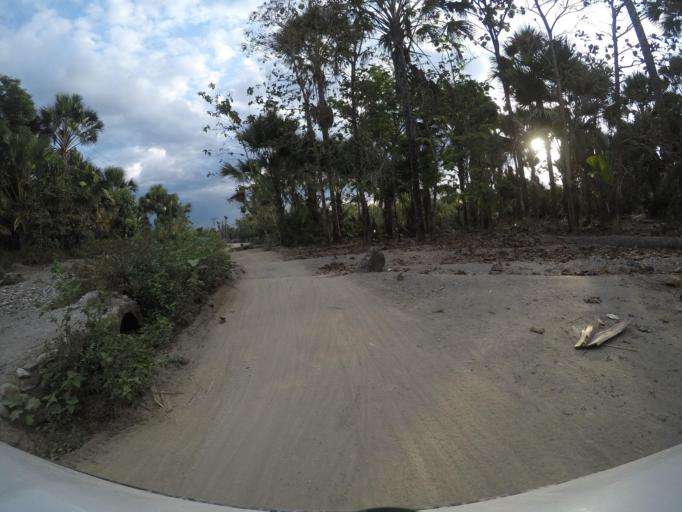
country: TL
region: Bobonaro
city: Maliana
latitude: -8.8645
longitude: 125.2155
